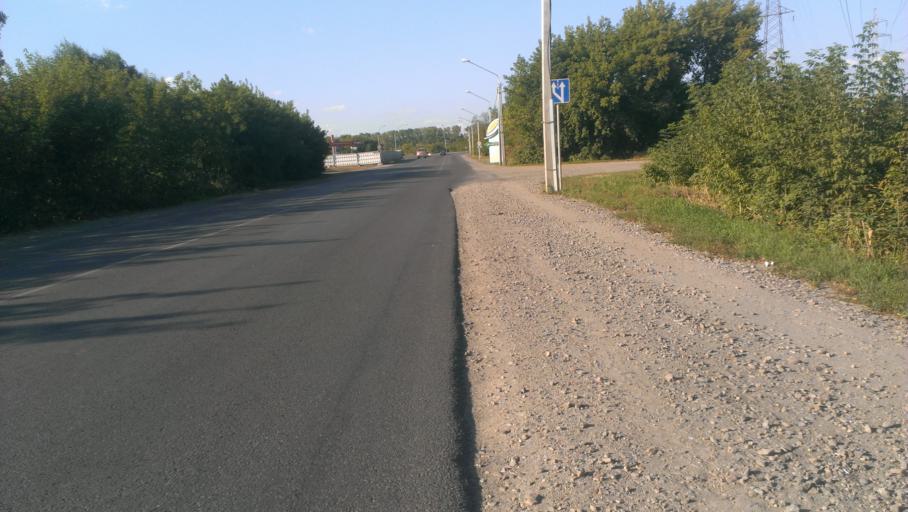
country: RU
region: Altai Krai
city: Novosilikatnyy
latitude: 53.3469
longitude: 83.6201
